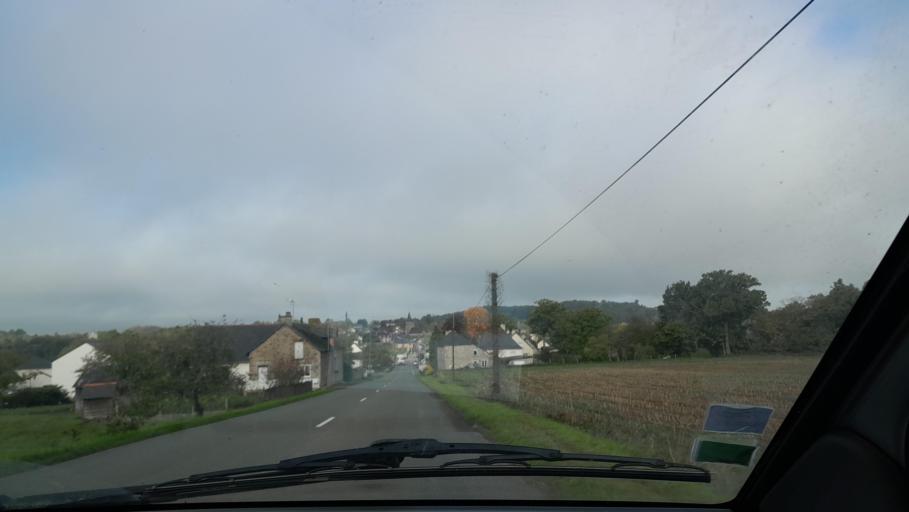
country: FR
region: Brittany
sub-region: Departement d'Ille-et-Vilaine
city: Luitre
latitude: 48.2627
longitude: -1.1358
